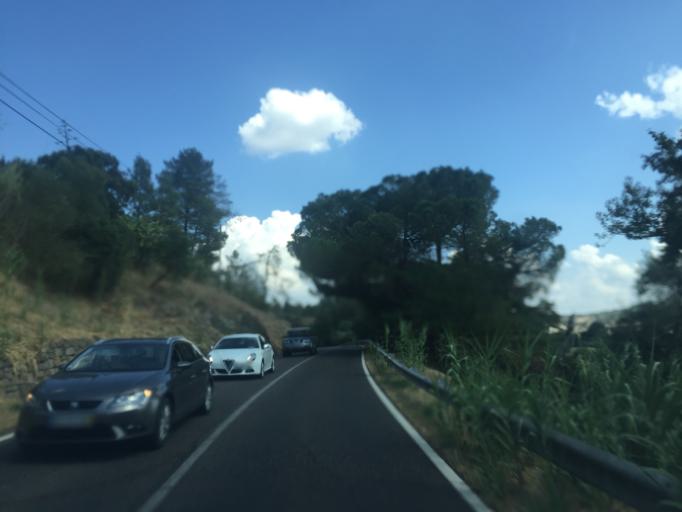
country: PT
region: Santarem
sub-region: Chamusca
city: Vila Nova da Barquinha
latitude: 39.4582
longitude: -8.4168
